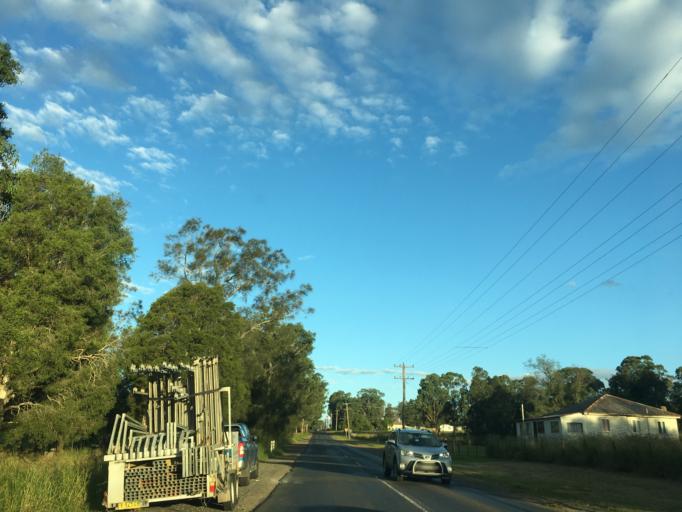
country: AU
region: New South Wales
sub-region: Campbelltown Municipality
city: Denham Court
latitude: -33.9630
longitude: 150.8064
